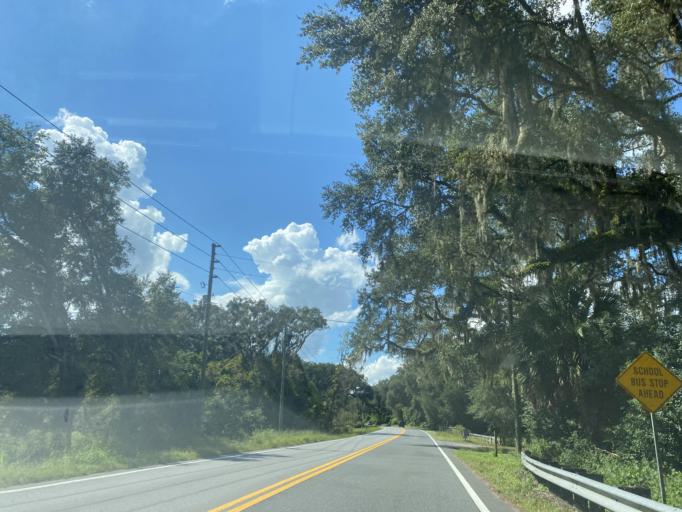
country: US
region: Florida
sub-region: Lake County
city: Lady Lake
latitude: 28.9828
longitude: -81.8905
